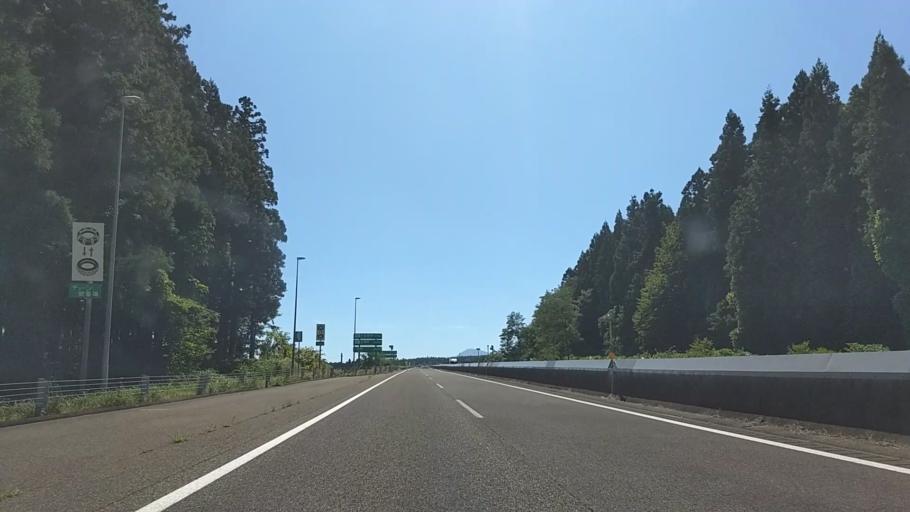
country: JP
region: Niigata
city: Arai
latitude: 36.9585
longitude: 138.2193
